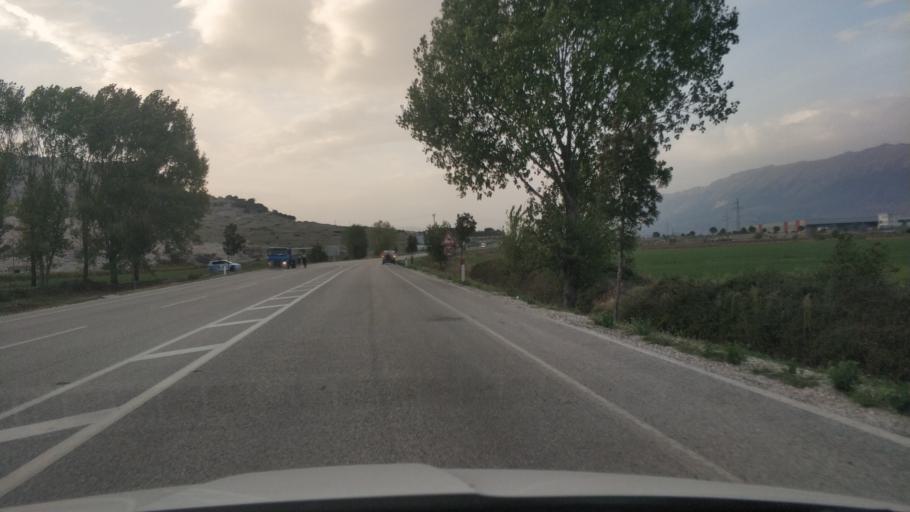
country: AL
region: Gjirokaster
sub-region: Rrethi i Gjirokastres
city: Libohove
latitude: 39.9682
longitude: 20.2385
